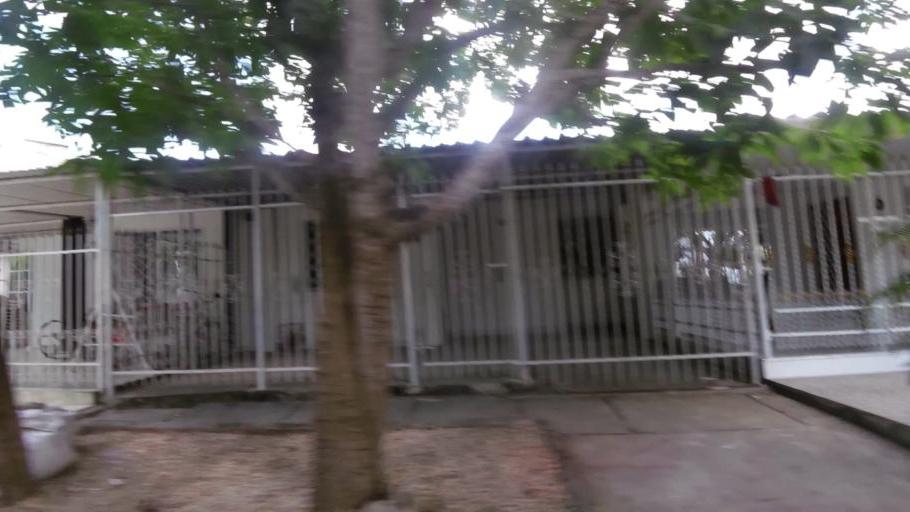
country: CO
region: Bolivar
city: Cartagena
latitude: 10.3708
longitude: -75.4615
